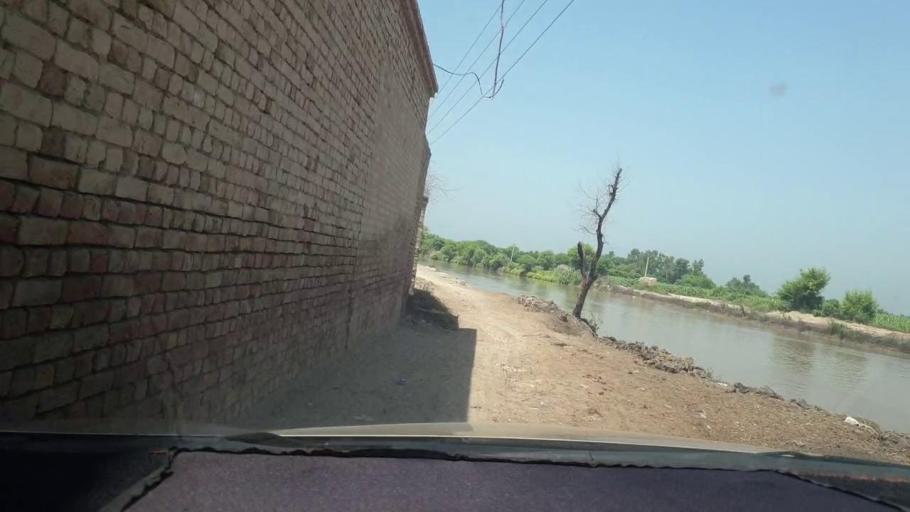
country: PK
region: Sindh
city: Kambar
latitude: 27.6072
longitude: 68.0872
